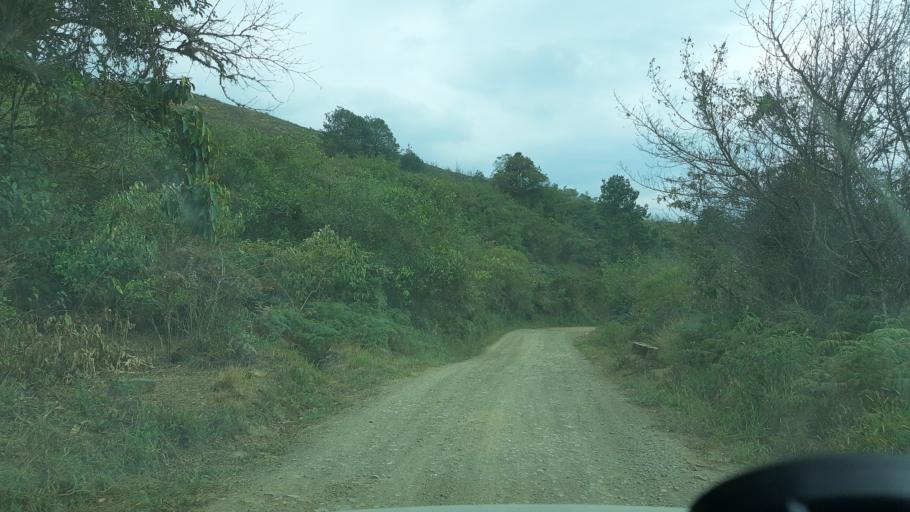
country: CO
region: Boyaca
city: Somondoco
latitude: 4.9845
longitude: -73.3750
